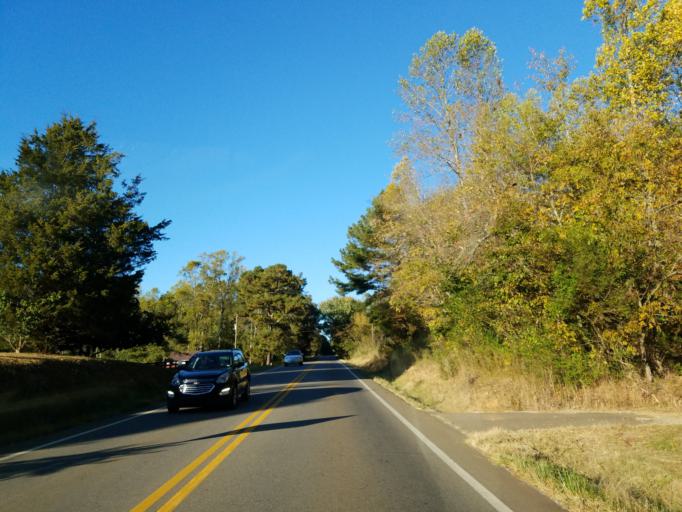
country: US
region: Georgia
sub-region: Dawson County
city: Dawsonville
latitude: 34.4231
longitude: -84.1931
